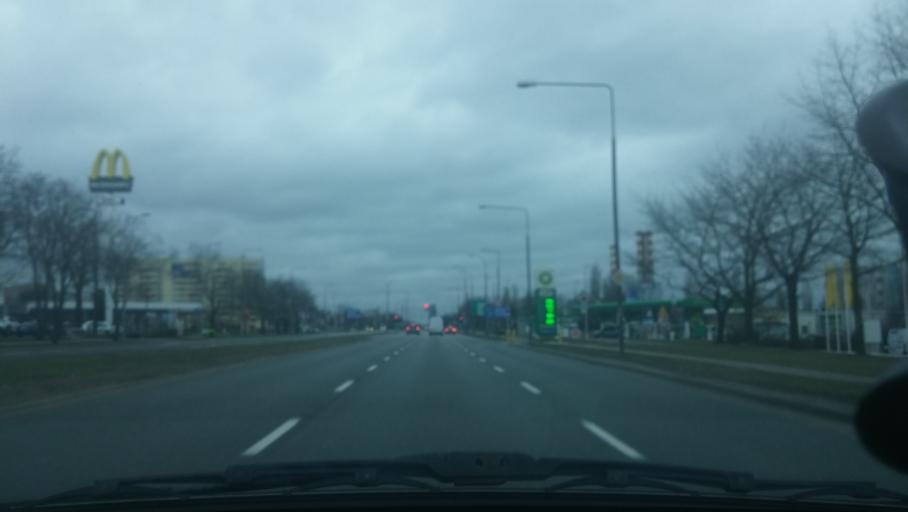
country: PL
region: Masovian Voivodeship
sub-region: Warszawa
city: Bemowo
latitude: 52.2194
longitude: 20.9135
